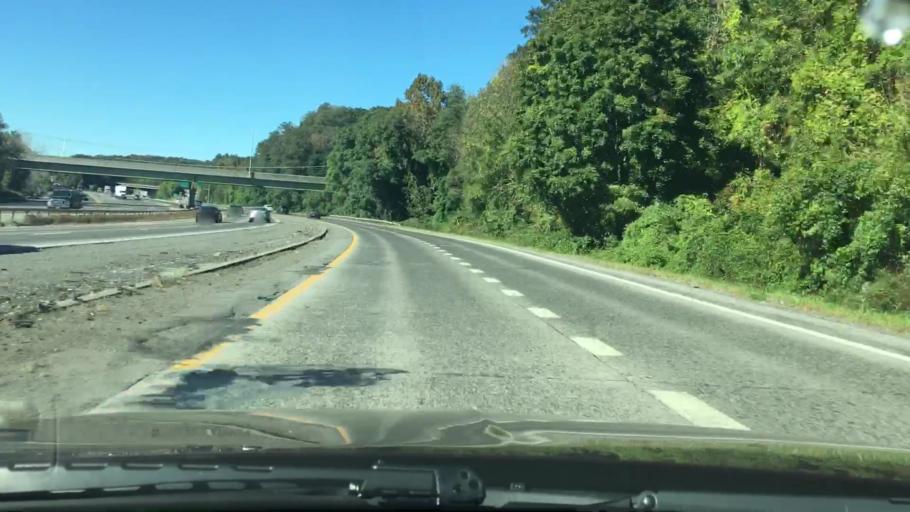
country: US
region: New York
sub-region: Westchester County
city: Katonah
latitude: 41.2589
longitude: -73.6791
